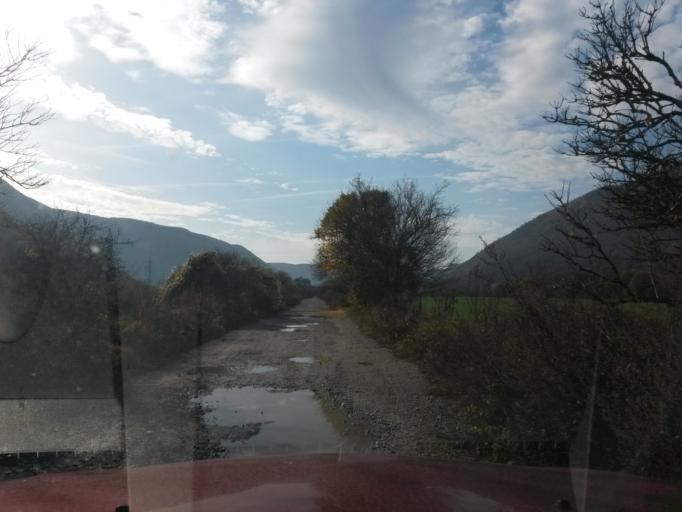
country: SK
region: Kosicky
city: Roznava
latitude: 48.6101
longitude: 20.4848
